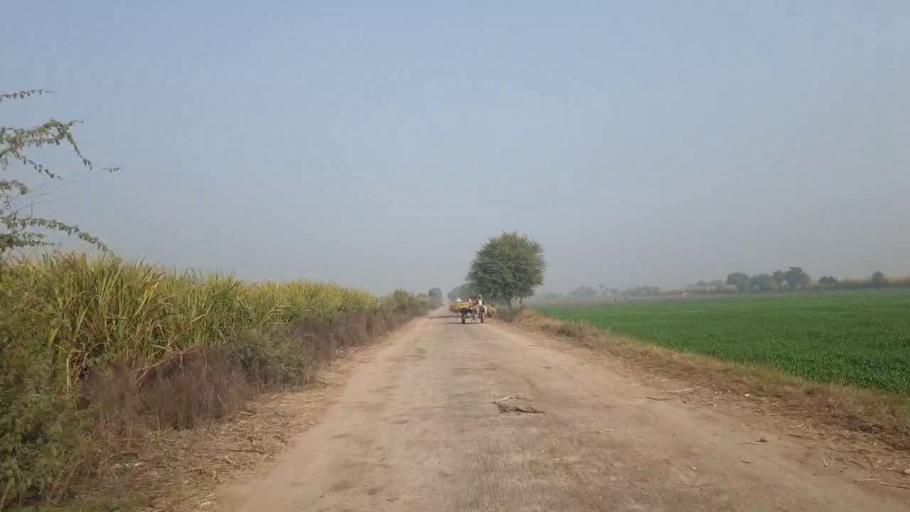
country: PK
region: Sindh
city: Tando Adam
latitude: 25.8130
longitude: 68.6153
